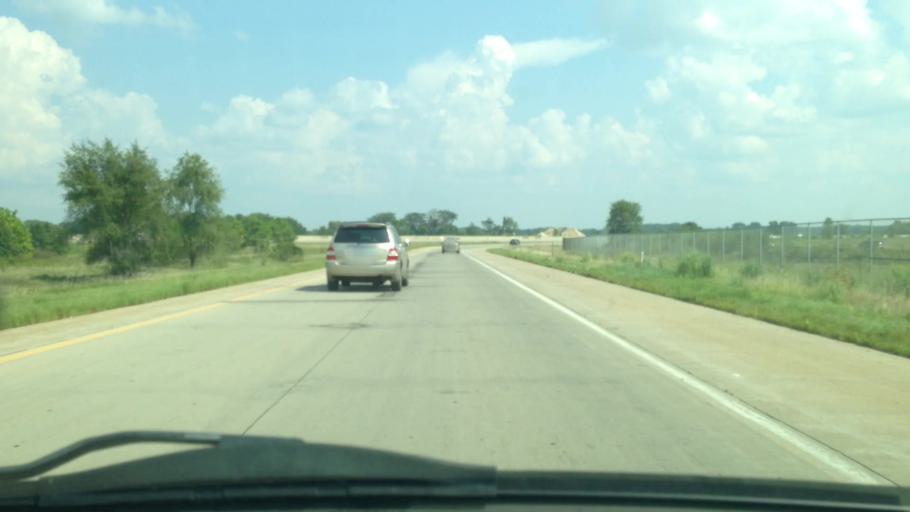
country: US
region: Iowa
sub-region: Black Hawk County
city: Cedar Falls
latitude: 42.5358
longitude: -92.3917
